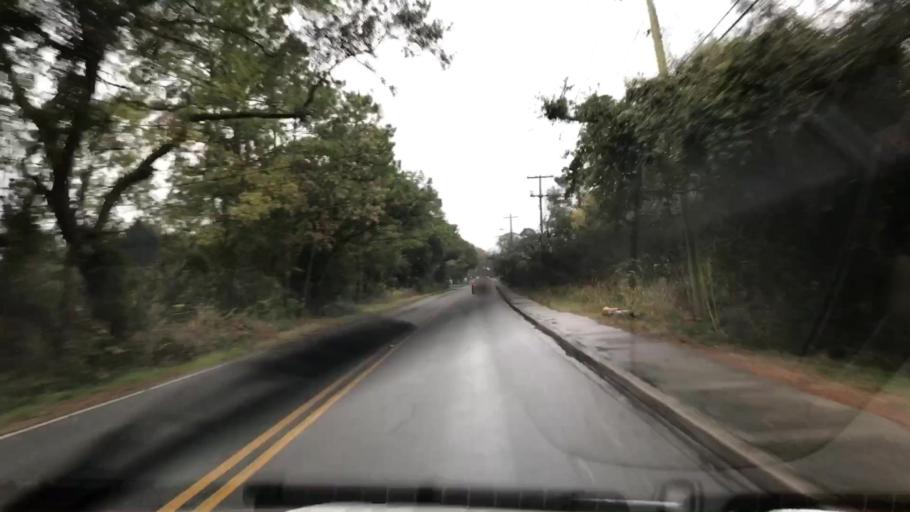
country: US
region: South Carolina
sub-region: Charleston County
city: North Charleston
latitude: 32.8138
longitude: -80.0139
